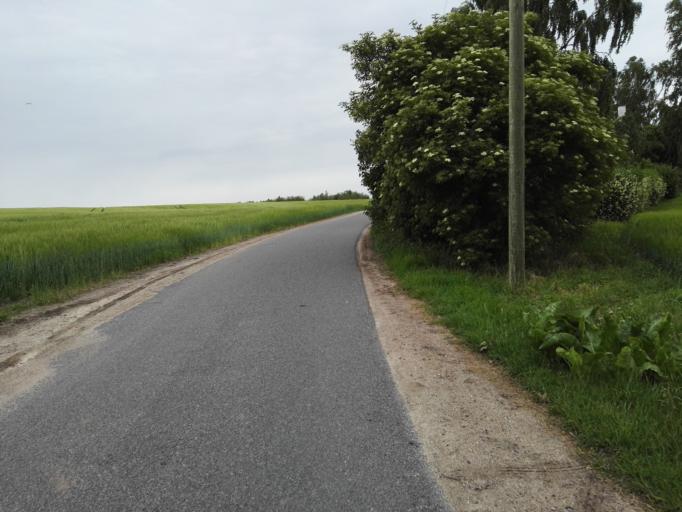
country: DK
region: Zealand
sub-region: Roskilde Kommune
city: Jyllinge
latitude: 55.7915
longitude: 12.1064
